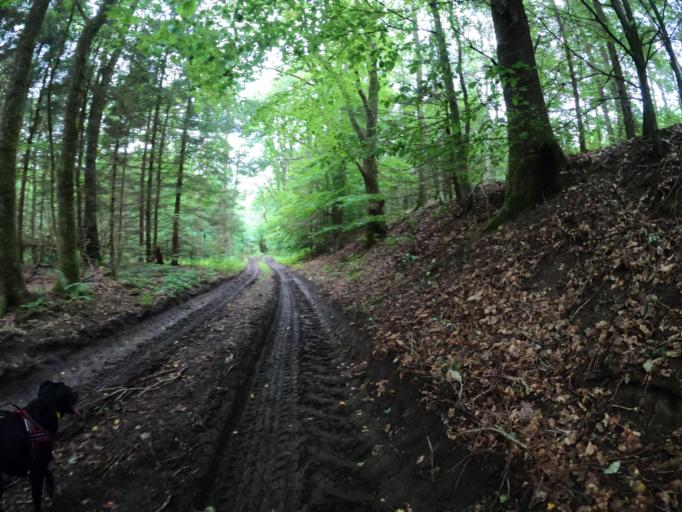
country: PL
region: West Pomeranian Voivodeship
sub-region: Powiat szczecinecki
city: Grzmiaca
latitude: 53.9719
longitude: 16.4403
